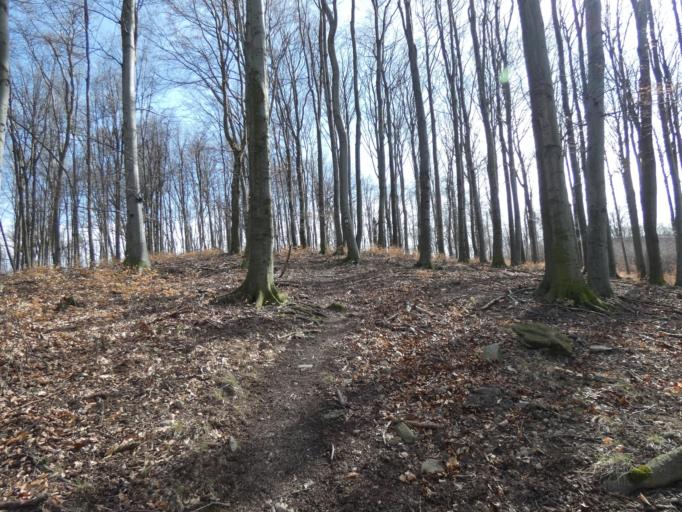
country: HU
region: Nograd
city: Diosjeno
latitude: 47.9735
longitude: 18.9556
